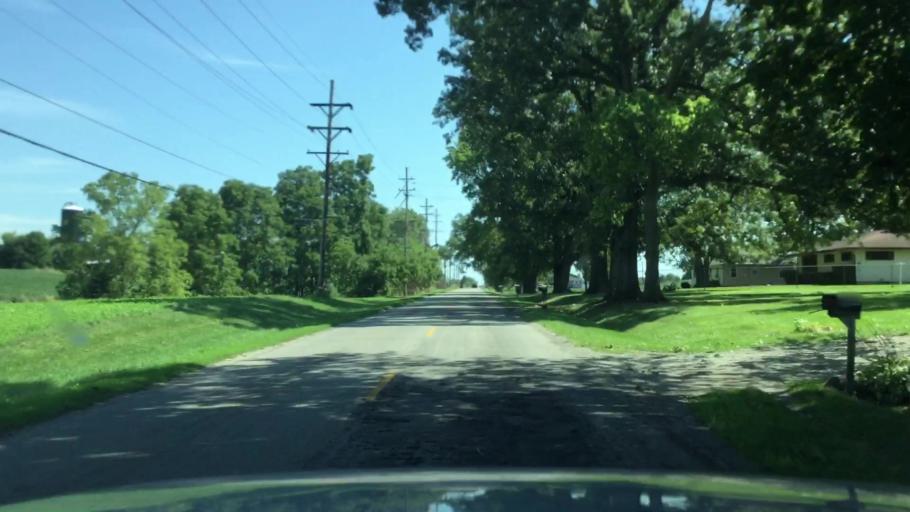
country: US
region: Michigan
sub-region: Lenawee County
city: Clinton
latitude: 42.0649
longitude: -83.9612
